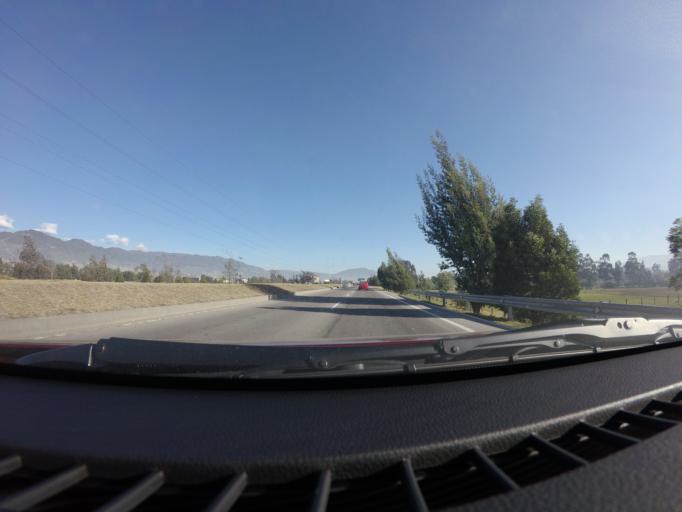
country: CO
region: Cundinamarca
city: Zipaquira
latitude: 5.0059
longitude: -73.9889
